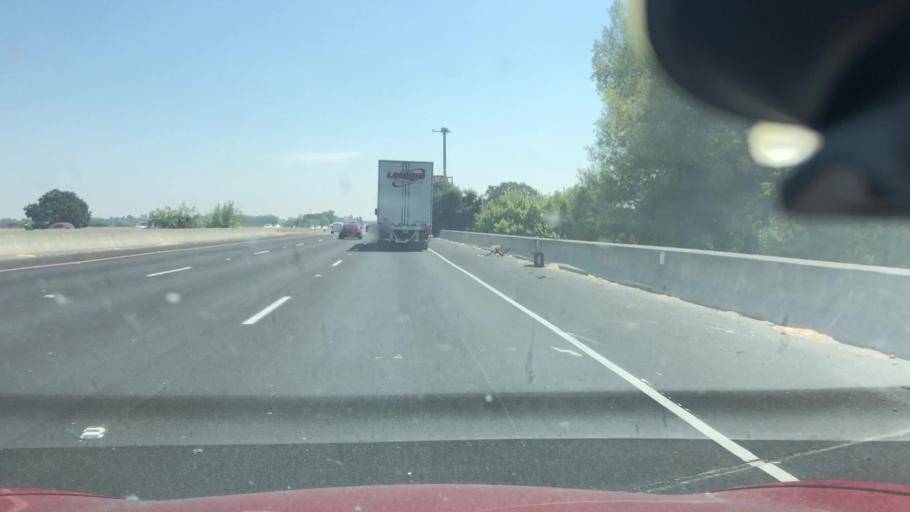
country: US
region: California
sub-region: Sacramento County
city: Parkway
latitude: 38.4395
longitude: -121.4904
